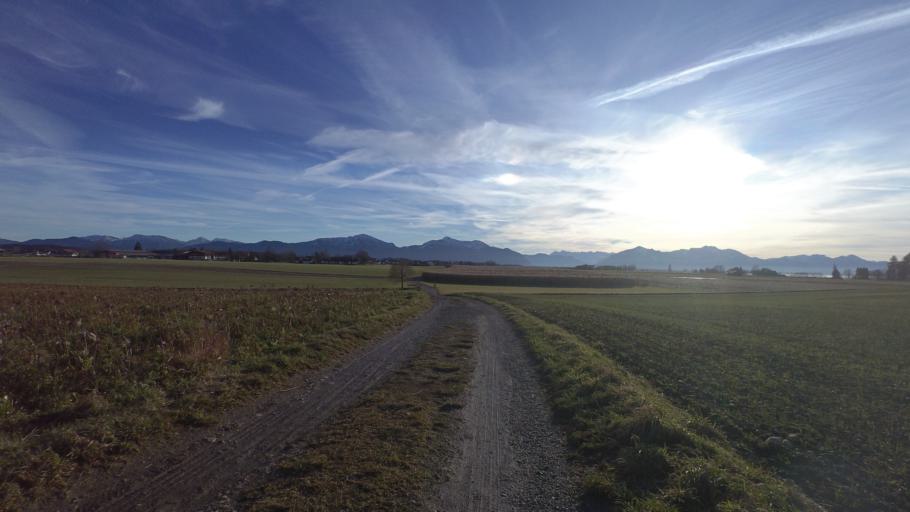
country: DE
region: Bavaria
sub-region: Upper Bavaria
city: Chieming
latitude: 47.9039
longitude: 12.5343
